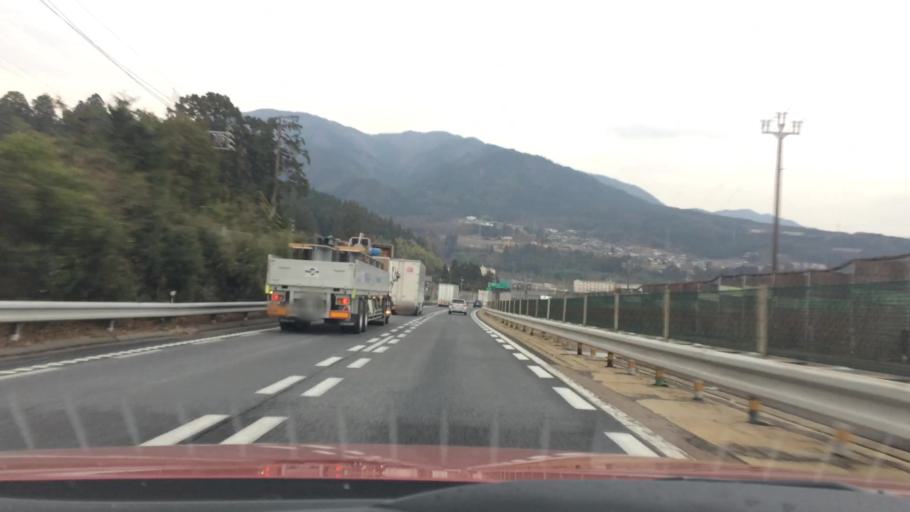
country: JP
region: Gifu
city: Nakatsugawa
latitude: 35.4834
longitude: 137.5103
